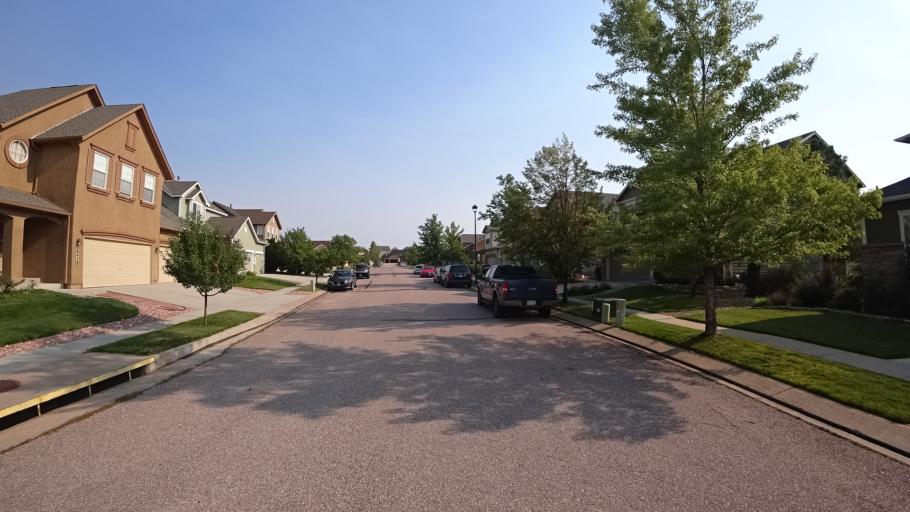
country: US
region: Colorado
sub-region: El Paso County
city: Black Forest
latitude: 38.9534
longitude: -104.7200
